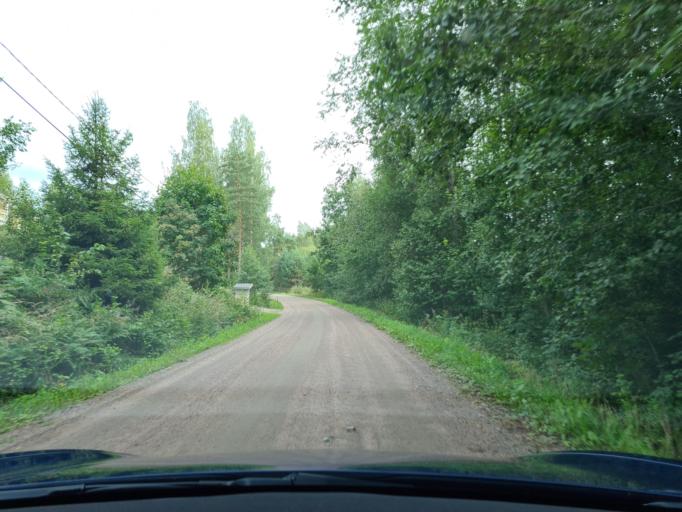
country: FI
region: Uusimaa
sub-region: Helsinki
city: Vihti
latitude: 60.4231
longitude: 24.4746
